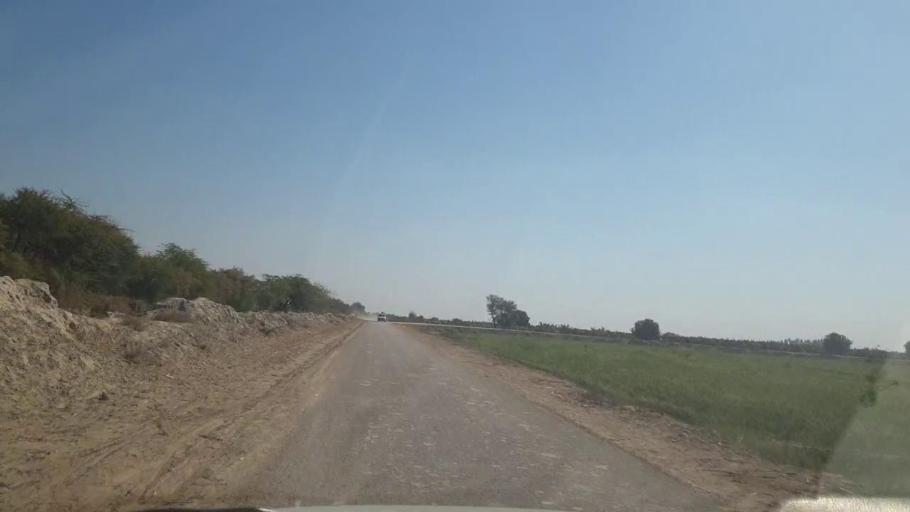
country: PK
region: Sindh
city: Mirpur Khas
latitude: 25.4615
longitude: 69.1807
